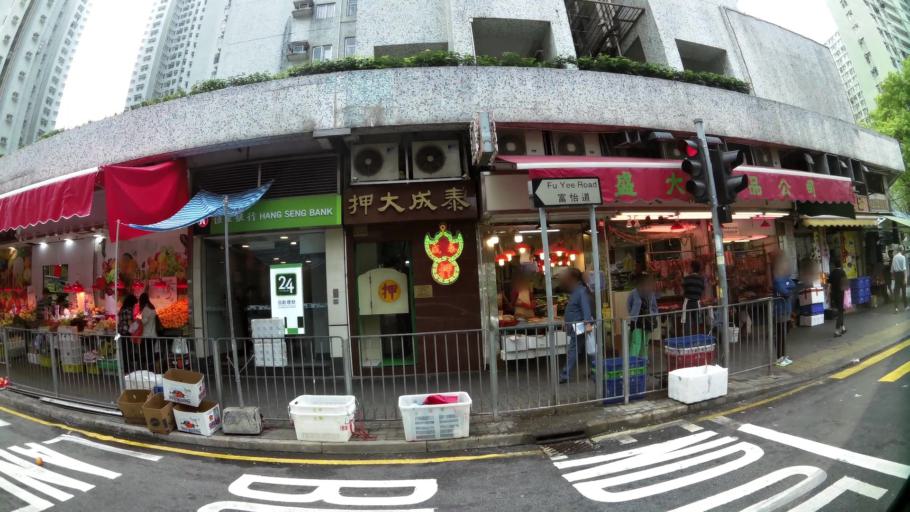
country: HK
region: Wanchai
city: Wan Chai
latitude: 22.2631
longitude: 114.2497
